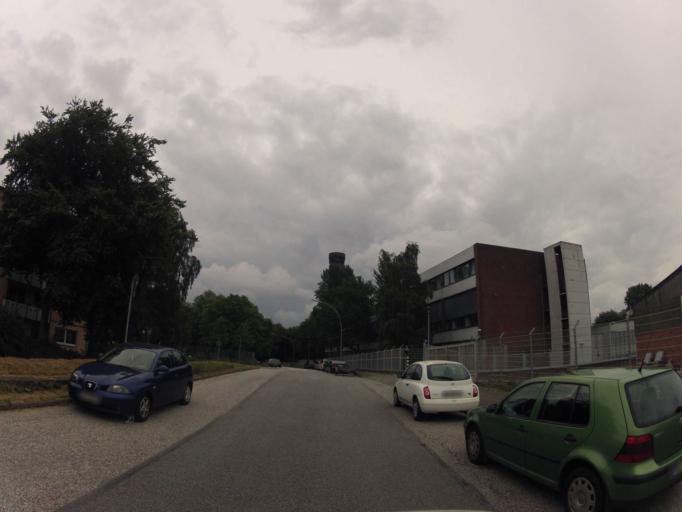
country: DE
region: Hamburg
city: Rothenburgsort
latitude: 53.5324
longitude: 10.0387
